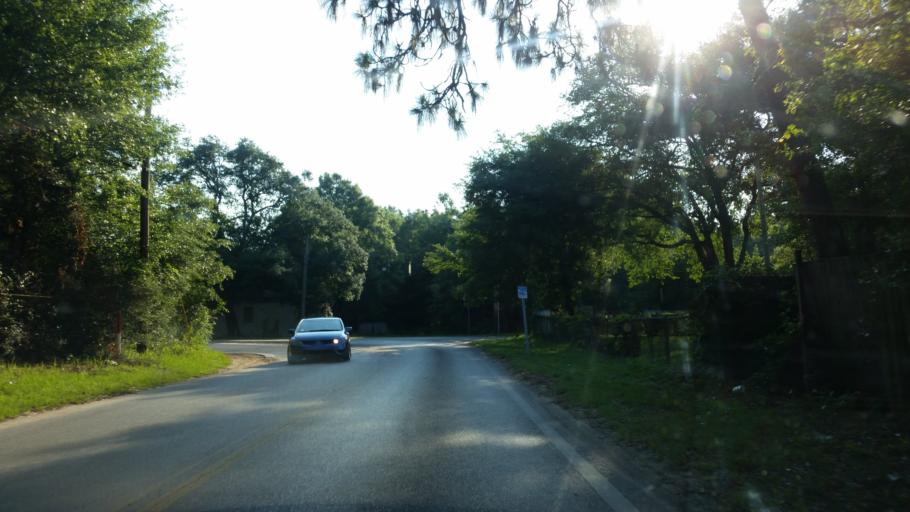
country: US
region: Florida
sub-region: Escambia County
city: Ensley
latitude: 30.4974
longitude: -87.2687
